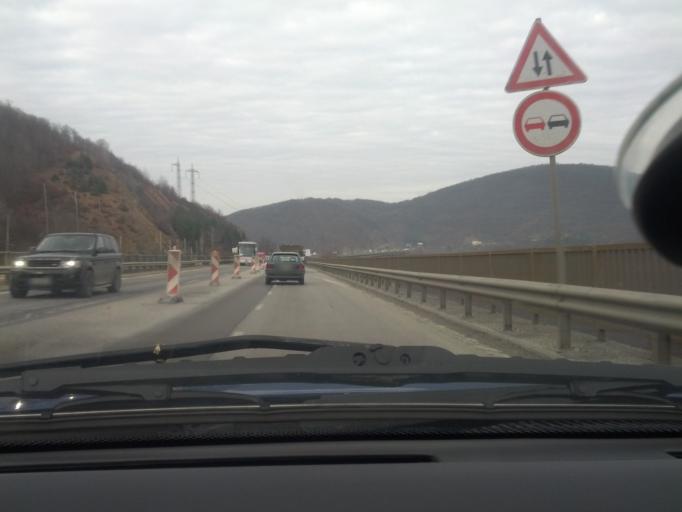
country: BG
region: Sofiya
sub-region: Obshtina Botevgrad
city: Botevgrad
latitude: 42.8186
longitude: 23.7980
